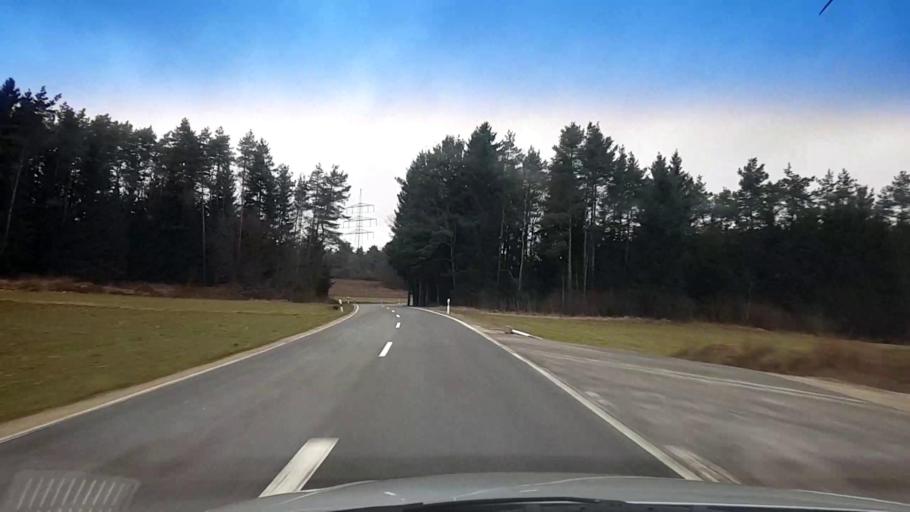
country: DE
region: Bavaria
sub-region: Upper Franconia
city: Wattendorf
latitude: 50.0157
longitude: 11.1293
